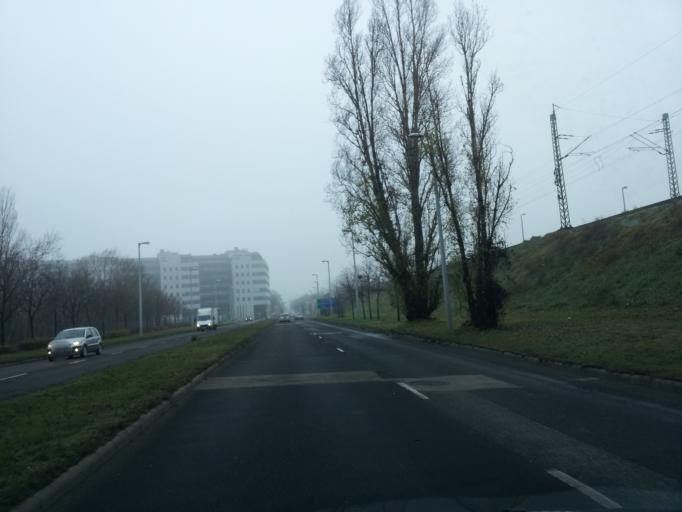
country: HU
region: Budapest
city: Budapest IX. keruelet
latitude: 47.4687
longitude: 19.0566
